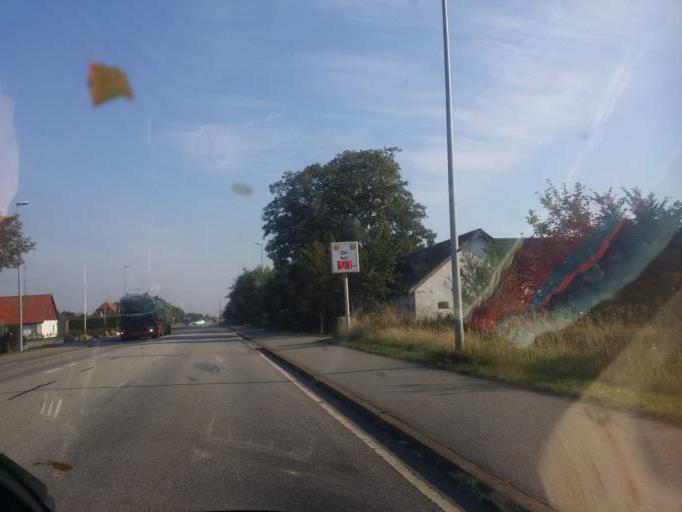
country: DK
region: South Denmark
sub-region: Tonder Kommune
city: Sherrebek
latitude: 55.2306
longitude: 8.7245
